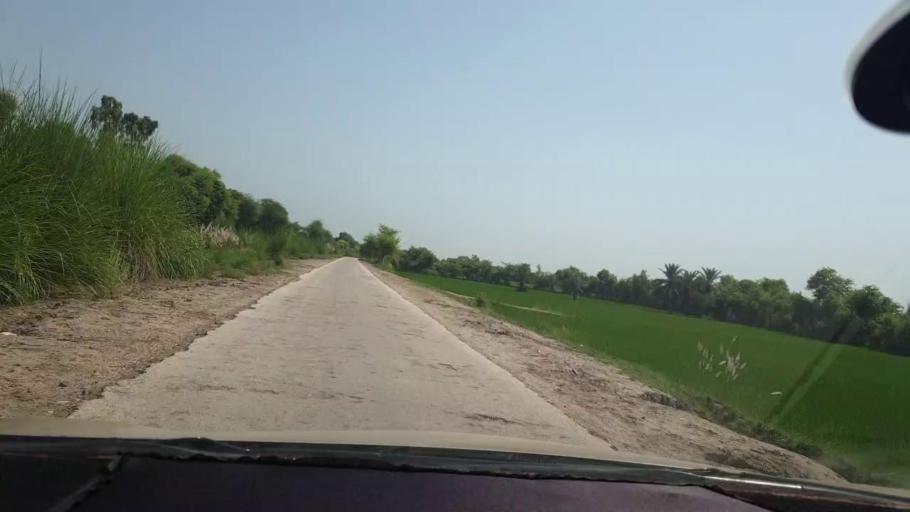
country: PK
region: Sindh
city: Kambar
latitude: 27.5140
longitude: 68.0112
